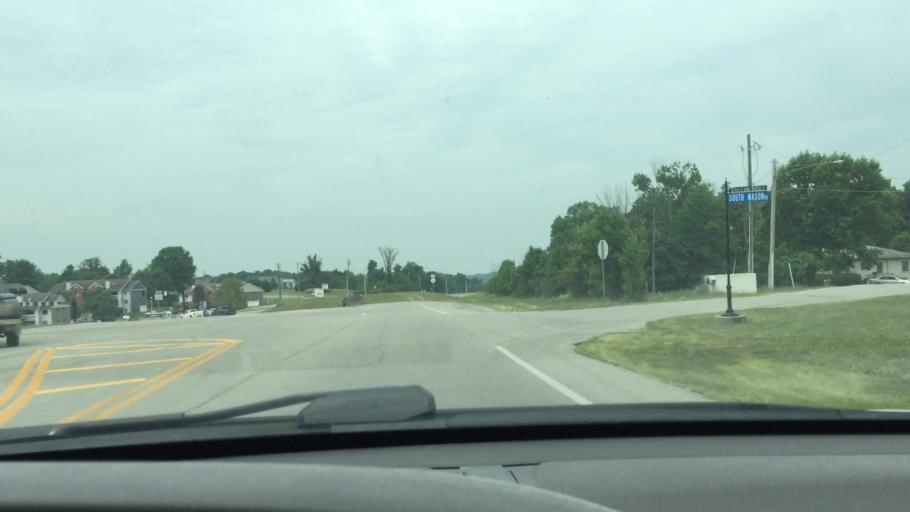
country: US
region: Kentucky
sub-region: Kenton County
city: Taylor Mill
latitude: 39.0181
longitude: -84.5080
